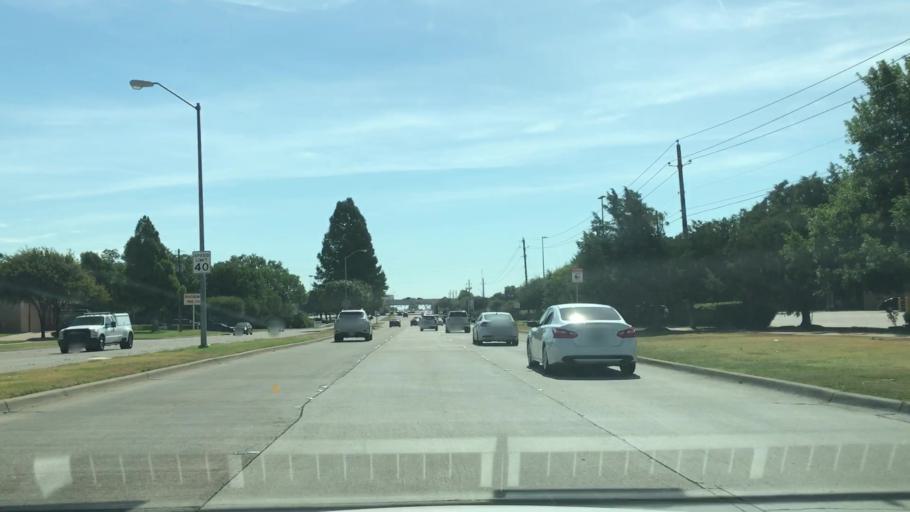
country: US
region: Texas
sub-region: Collin County
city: Plano
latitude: 33.0574
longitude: -96.6989
